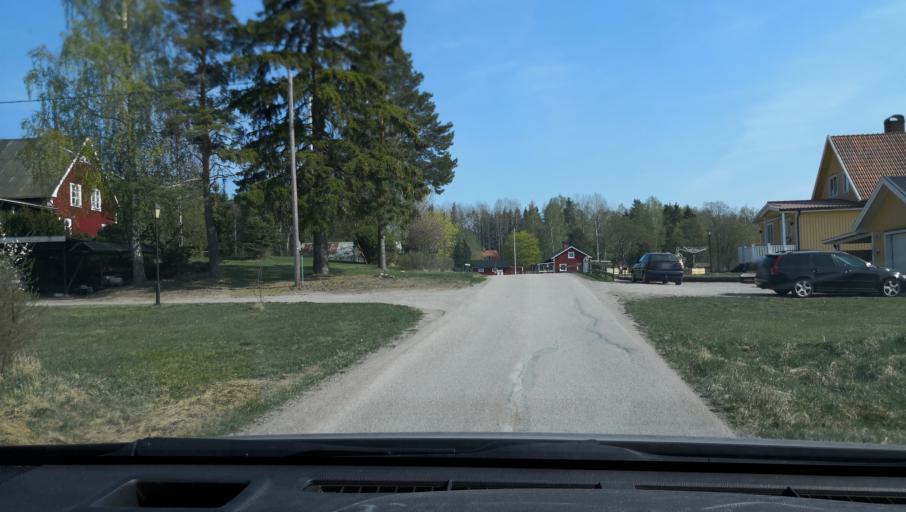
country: SE
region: Vaestmanland
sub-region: Sala Kommun
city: Sala
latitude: 60.0071
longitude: 16.7077
